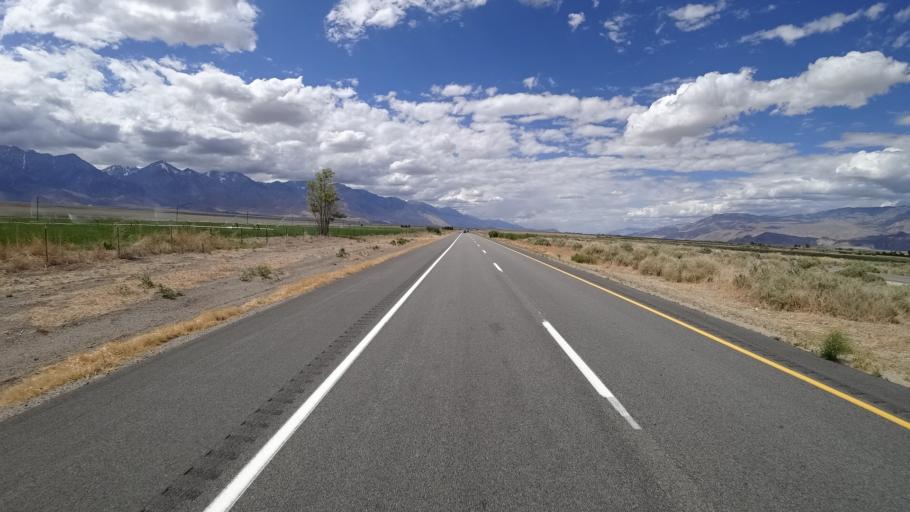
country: US
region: California
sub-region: Inyo County
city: Lone Pine
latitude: 36.7497
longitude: -118.1614
